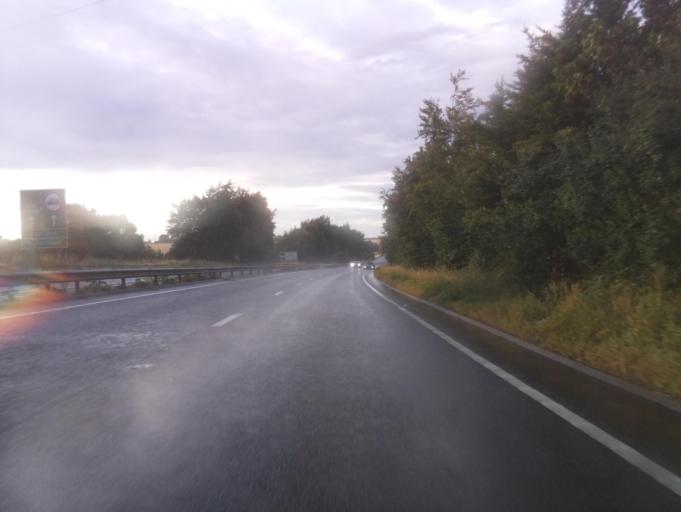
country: GB
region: England
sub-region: West Berkshire
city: Farnborough
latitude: 51.5259
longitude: -1.2948
